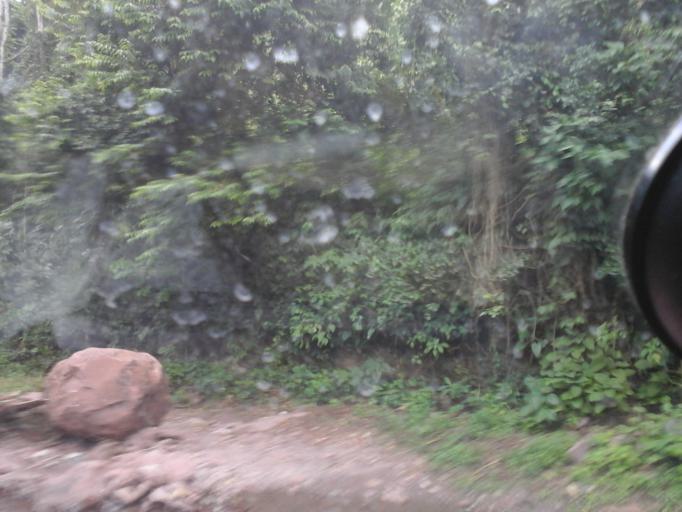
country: CO
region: Cesar
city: Manaure Balcon del Cesar
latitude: 10.2923
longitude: -73.0775
